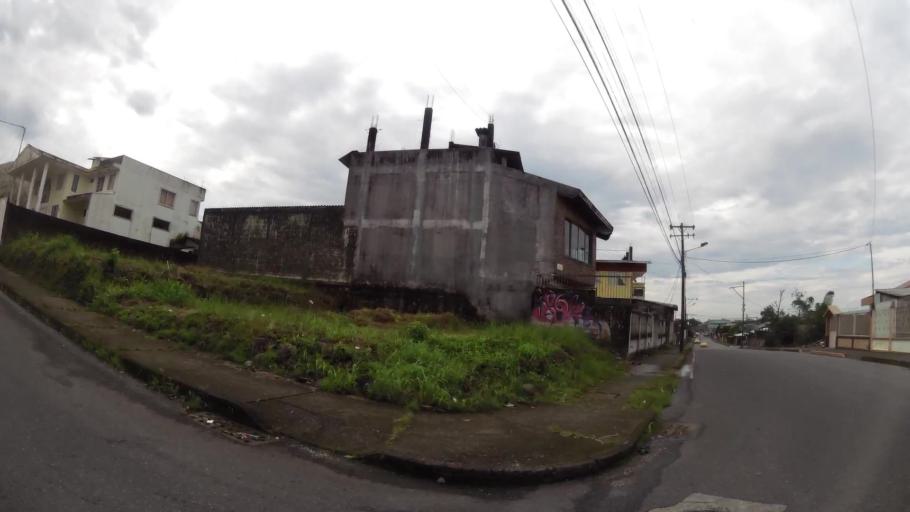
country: EC
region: Pastaza
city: Puyo
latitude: -1.4767
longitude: -78.0022
